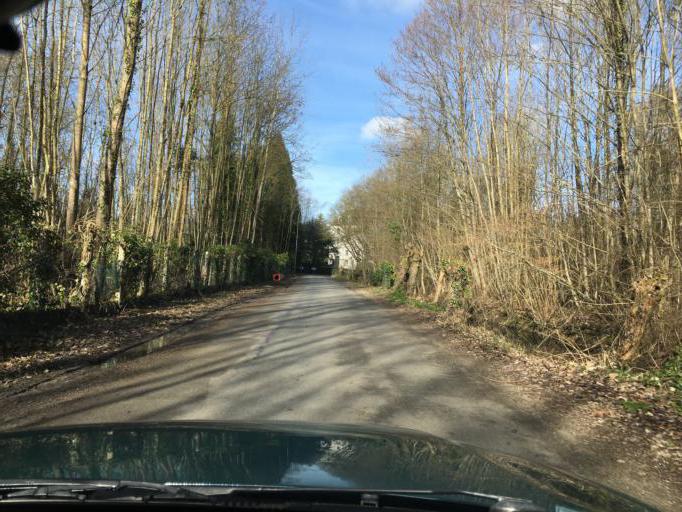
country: FR
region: Centre
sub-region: Departement du Loiret
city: Meung-sur-Loire
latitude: 47.8525
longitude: 1.7019
